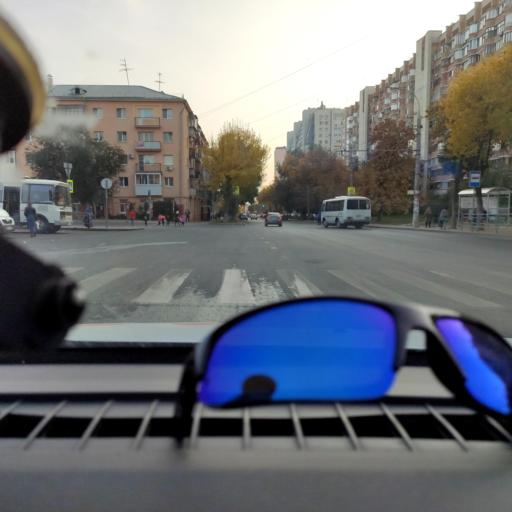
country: RU
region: Samara
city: Samara
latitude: 53.1929
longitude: 50.1224
